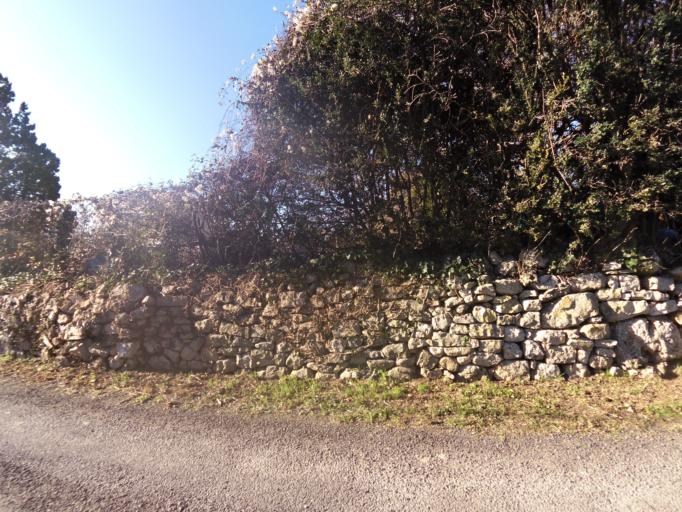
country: FR
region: Languedoc-Roussillon
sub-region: Departement du Gard
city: Quissac
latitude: 43.8951
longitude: 3.9990
